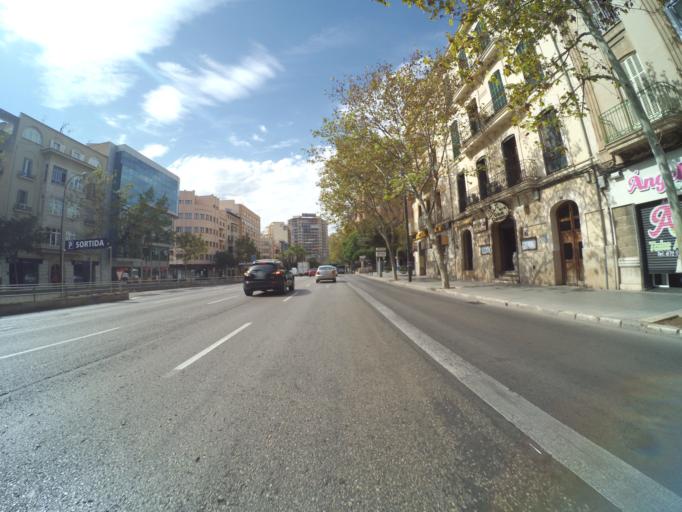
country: ES
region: Balearic Islands
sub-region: Illes Balears
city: Palma
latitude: 39.5780
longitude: 2.6508
